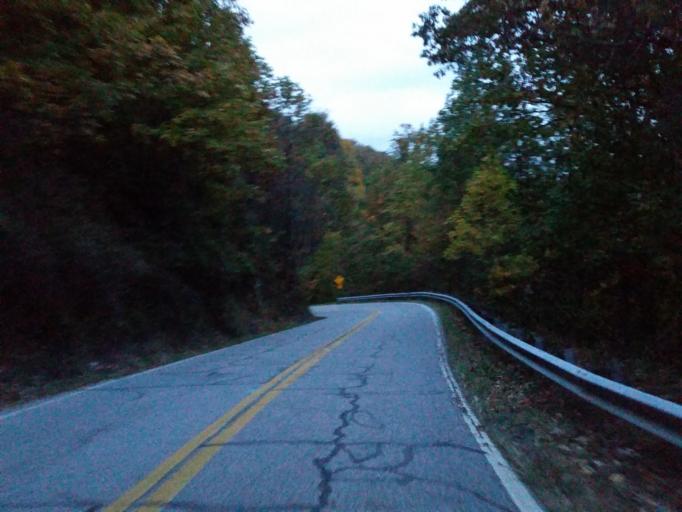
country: US
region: Georgia
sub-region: Lumpkin County
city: Dahlonega
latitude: 34.6469
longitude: -83.9652
